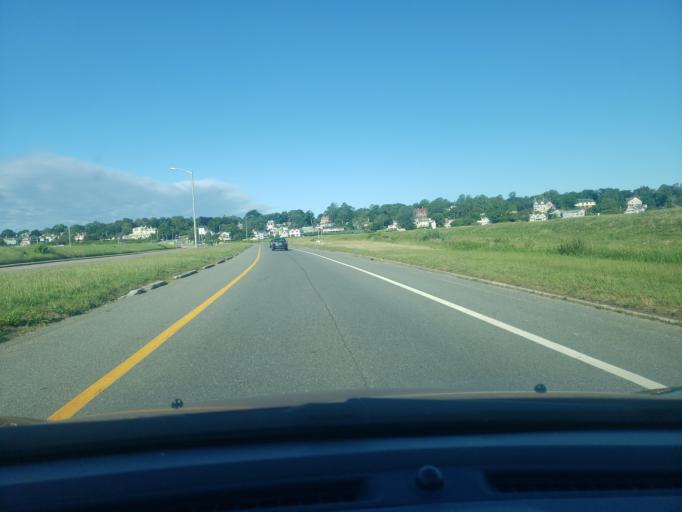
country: US
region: Rhode Island
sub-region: Newport County
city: Newport
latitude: 41.4888
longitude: -71.2919
